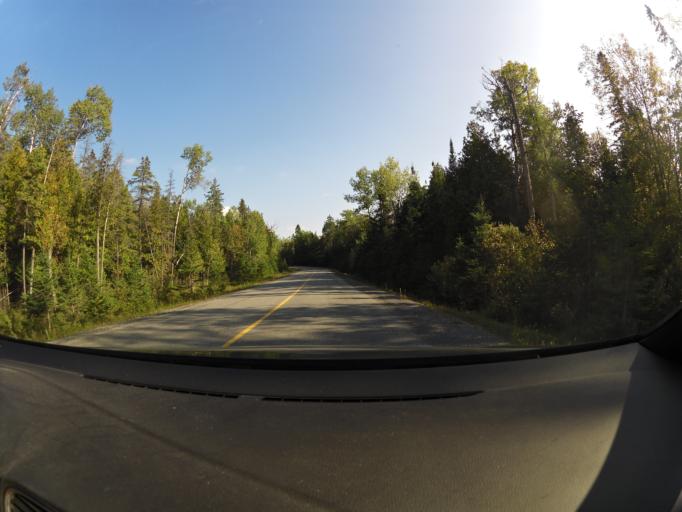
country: CA
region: Ontario
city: Arnprior
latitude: 45.4444
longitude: -76.2773
